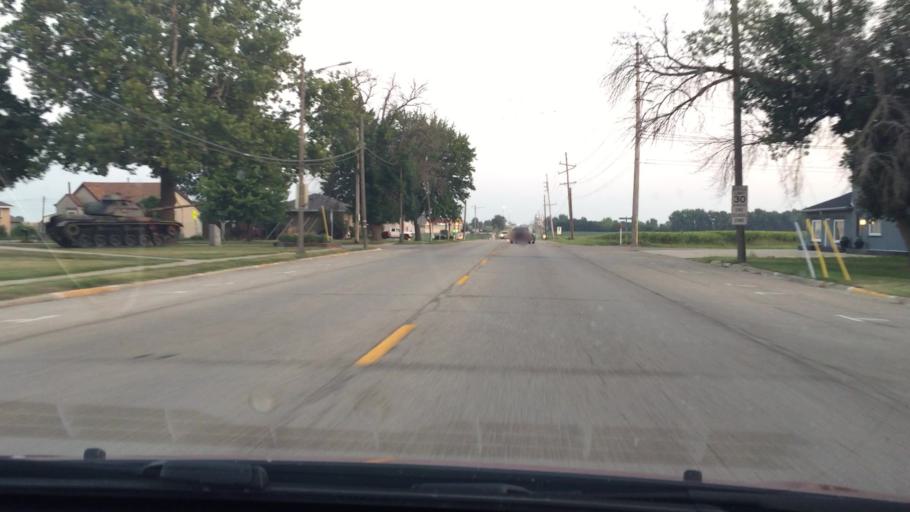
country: US
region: Illinois
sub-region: Bureau County
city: Ladd
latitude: 41.3795
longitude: -89.2190
